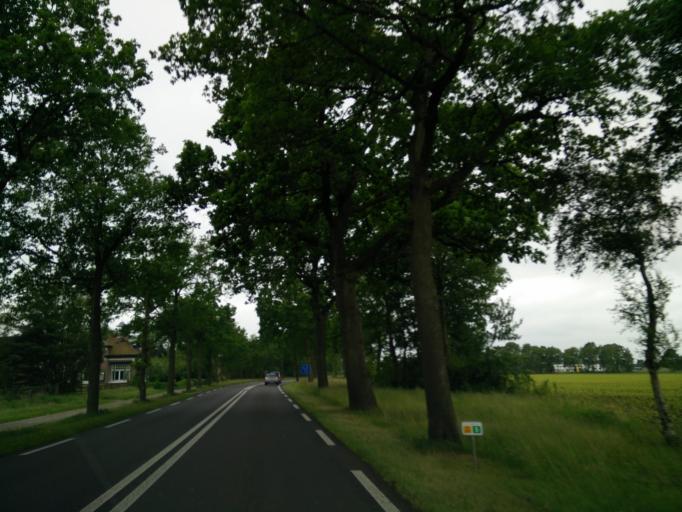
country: NL
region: Groningen
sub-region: Gemeente Groningen
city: Groningen
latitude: 53.1581
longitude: 6.4947
